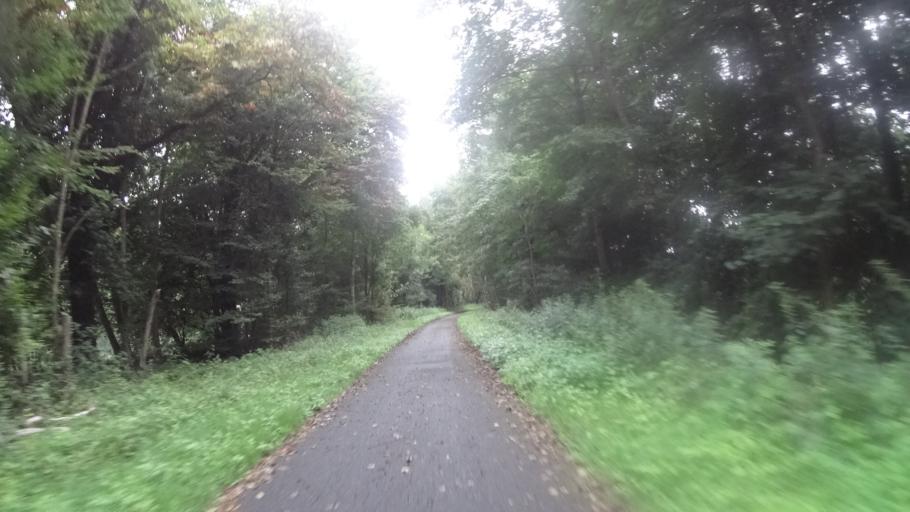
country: FR
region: Lorraine
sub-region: Departement de Meurthe-et-Moselle
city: Velaine-en-Haye
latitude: 48.6616
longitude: 6.0156
